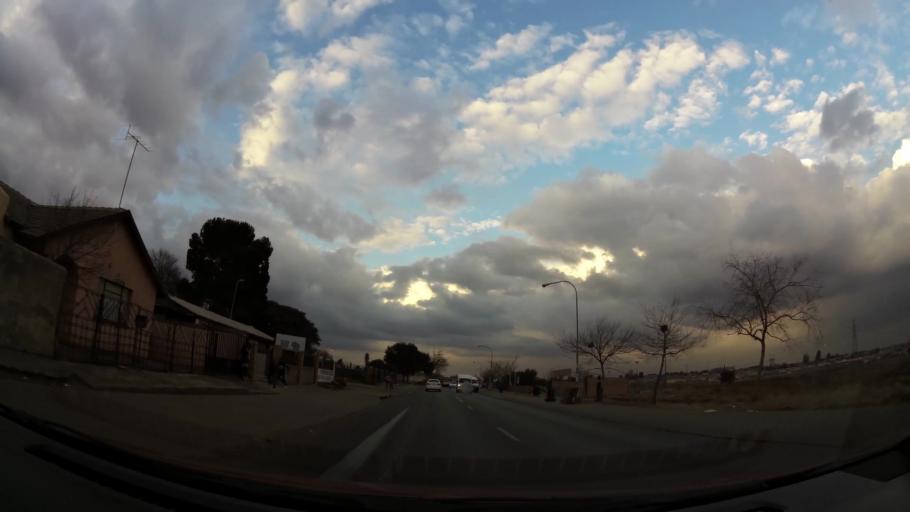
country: ZA
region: Gauteng
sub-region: City of Johannesburg Metropolitan Municipality
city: Soweto
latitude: -26.2407
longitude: 27.8430
